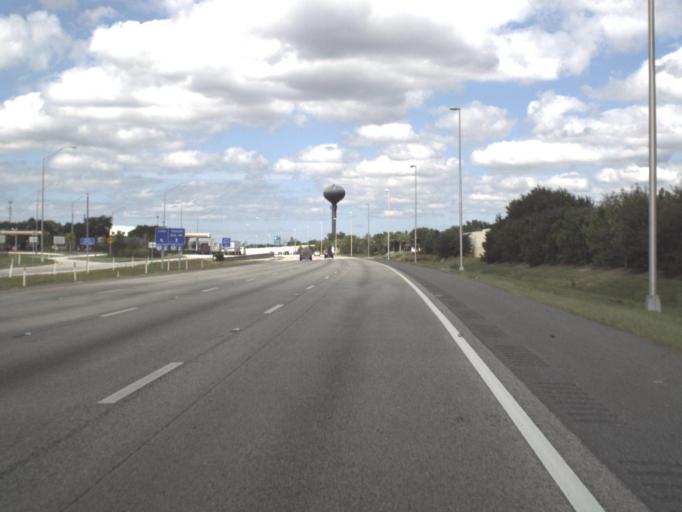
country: US
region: Florida
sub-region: Orange County
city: Gotha
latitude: 28.5127
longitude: -81.4956
